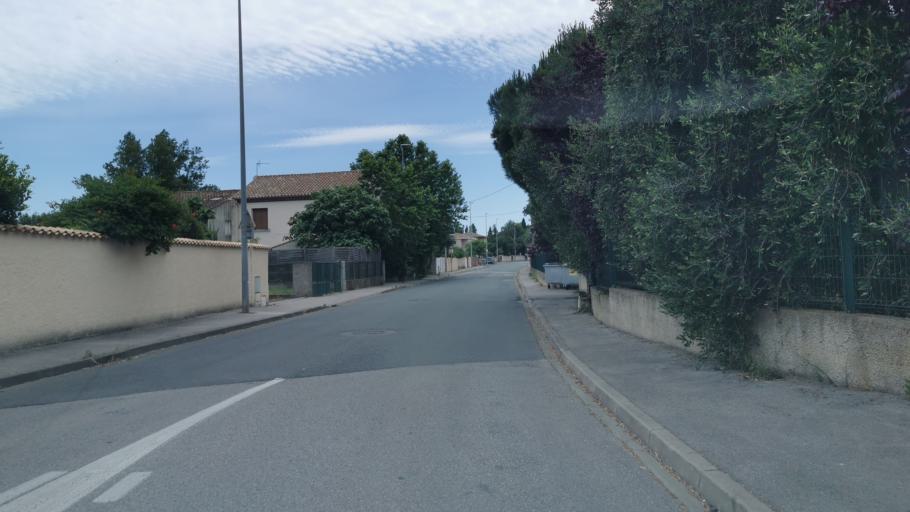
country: FR
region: Languedoc-Roussillon
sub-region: Departement de l'Aude
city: Narbonne
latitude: 43.1969
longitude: 3.0192
